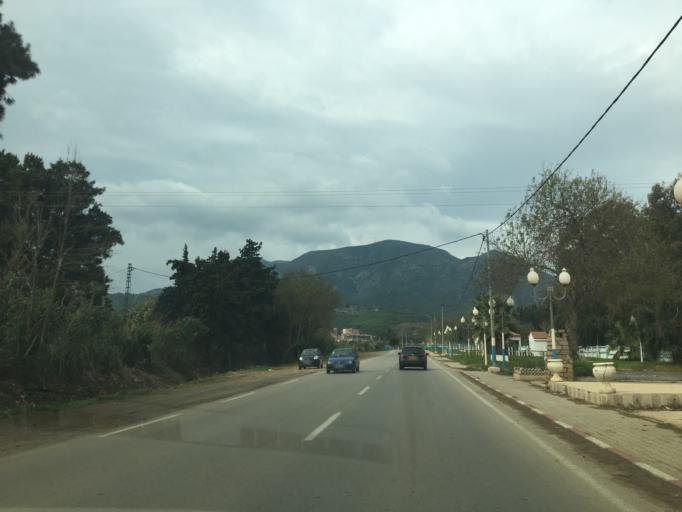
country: DZ
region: Tipaza
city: Tipasa
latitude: 36.5897
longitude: 2.4211
